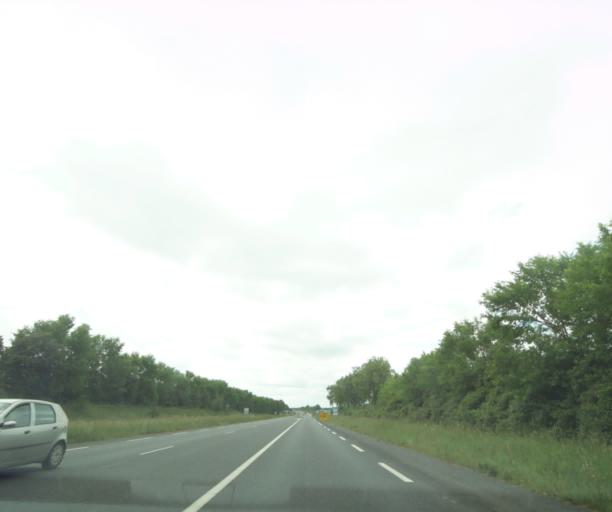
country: FR
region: Poitou-Charentes
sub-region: Departement des Deux-Sevres
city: Saint-Varent
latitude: 46.8508
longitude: -0.2088
